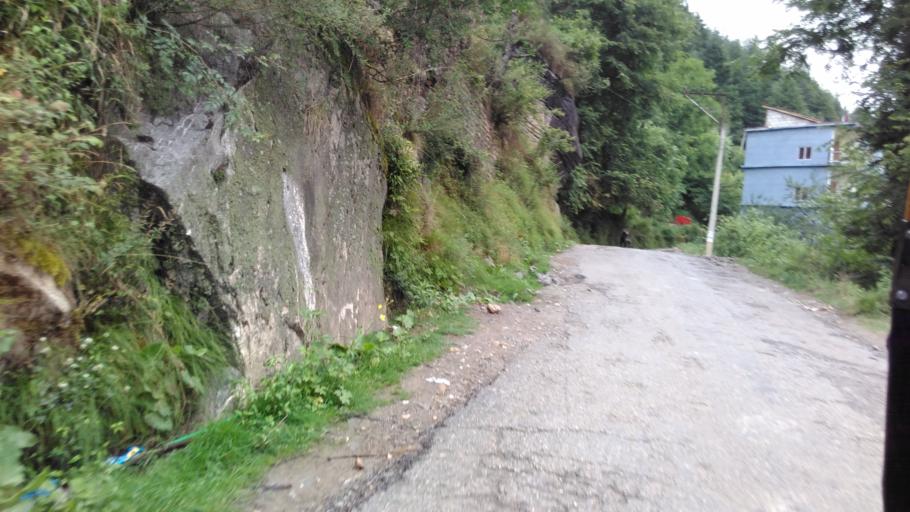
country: IN
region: Himachal Pradesh
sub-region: Kulu
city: Manali
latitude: 32.2282
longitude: 77.1848
